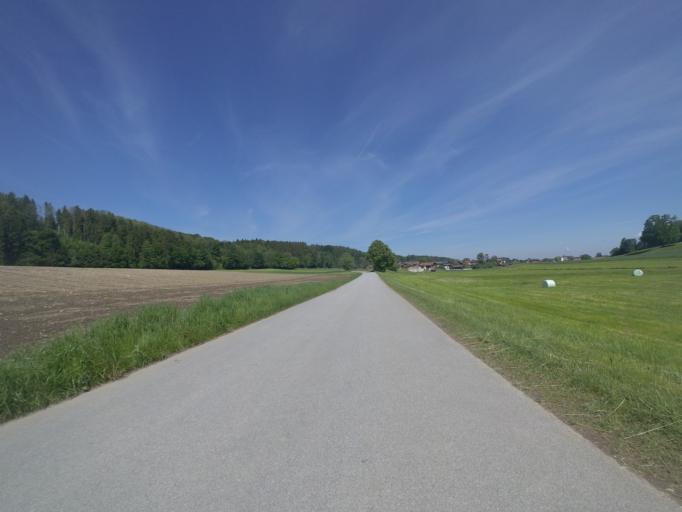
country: DE
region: Bavaria
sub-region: Upper Bavaria
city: Petting
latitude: 47.8902
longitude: 12.8240
